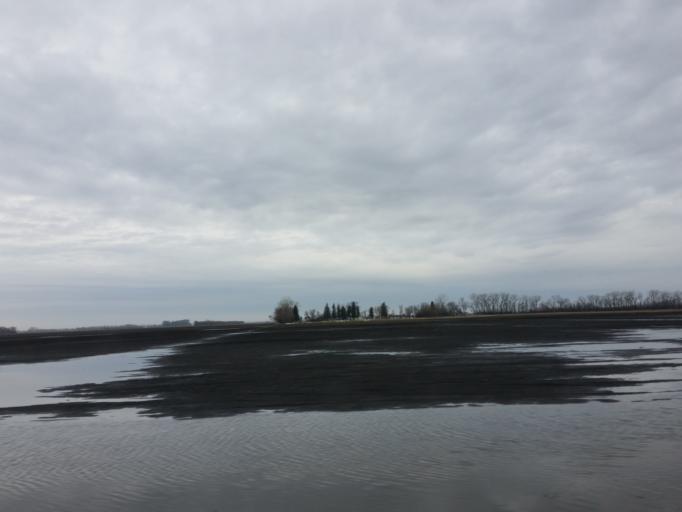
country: US
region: North Dakota
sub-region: Walsh County
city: Grafton
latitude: 48.3965
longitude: -97.4703
